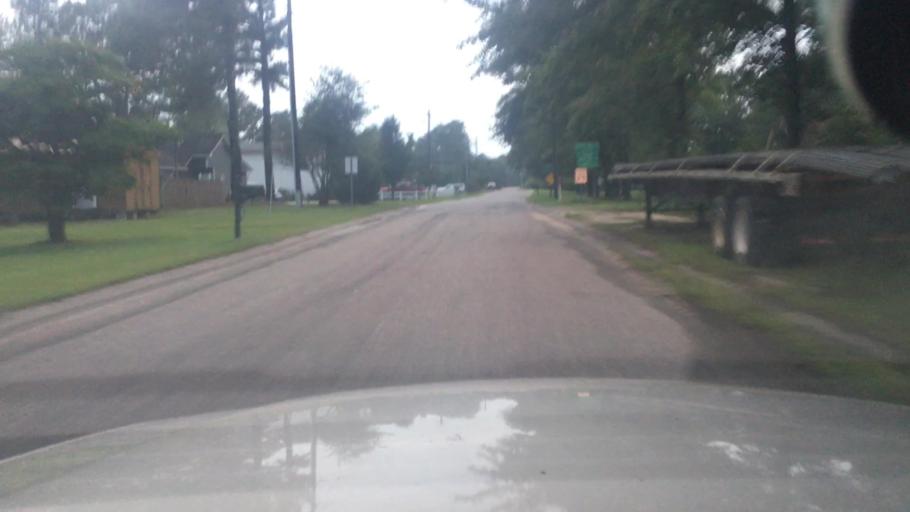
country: US
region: North Carolina
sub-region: Cumberland County
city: Hope Mills
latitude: 34.9623
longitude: -78.9376
